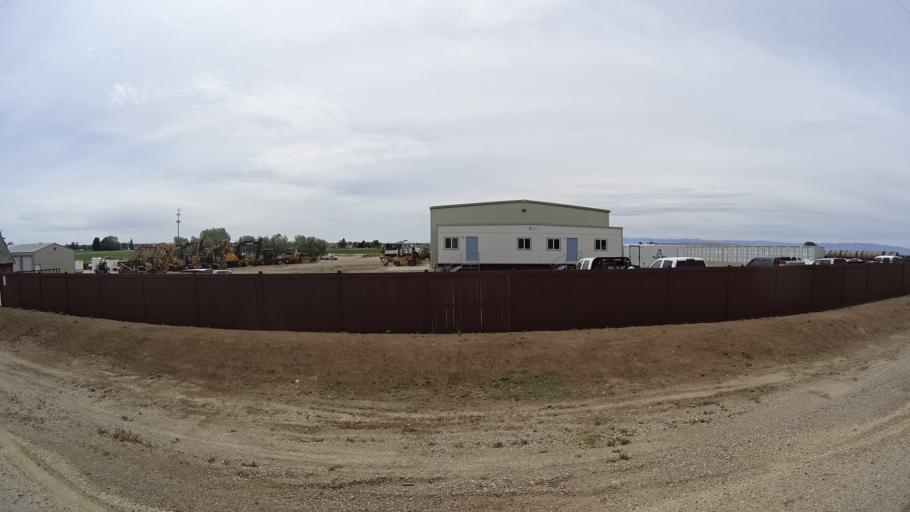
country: US
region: Idaho
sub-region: Ada County
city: Kuna
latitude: 43.5319
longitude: -116.3660
